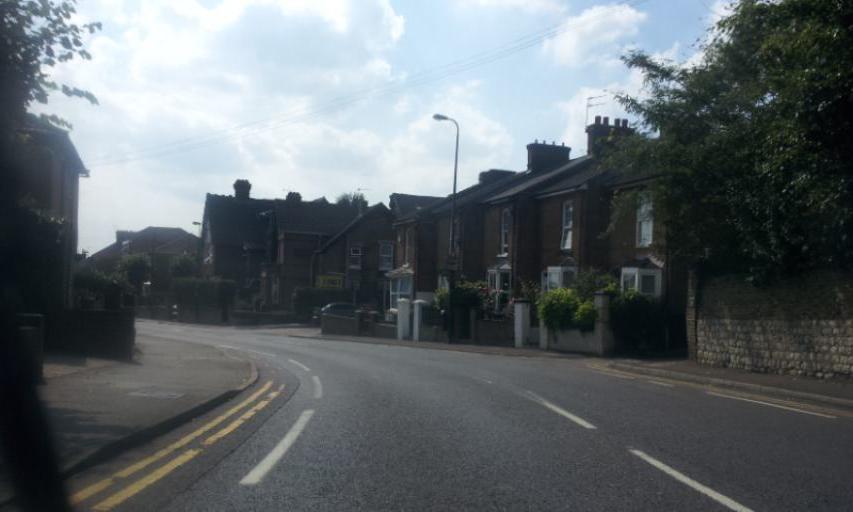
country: GB
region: England
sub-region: Kent
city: Maidstone
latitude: 51.2837
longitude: 0.5279
